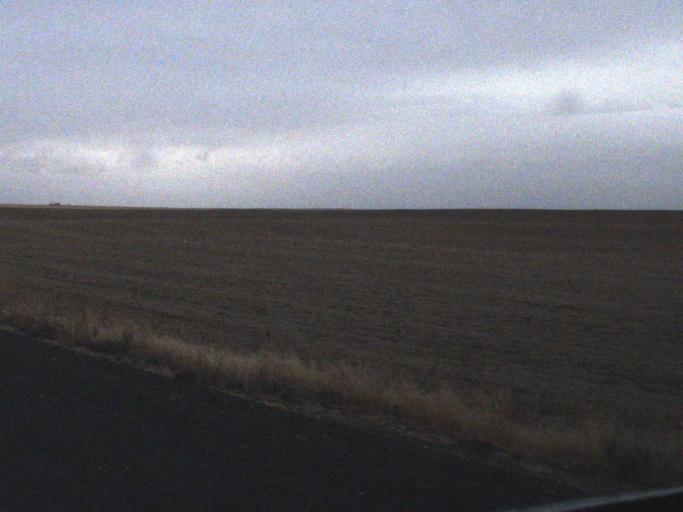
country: US
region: Washington
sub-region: Franklin County
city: Connell
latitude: 46.7944
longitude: -118.6470
